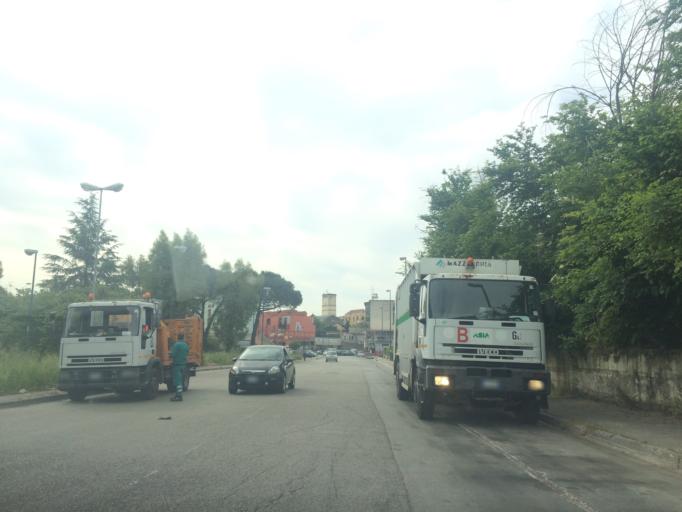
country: IT
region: Campania
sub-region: Provincia di Napoli
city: Mugnano di Napoli
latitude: 40.8927
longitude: 14.2276
